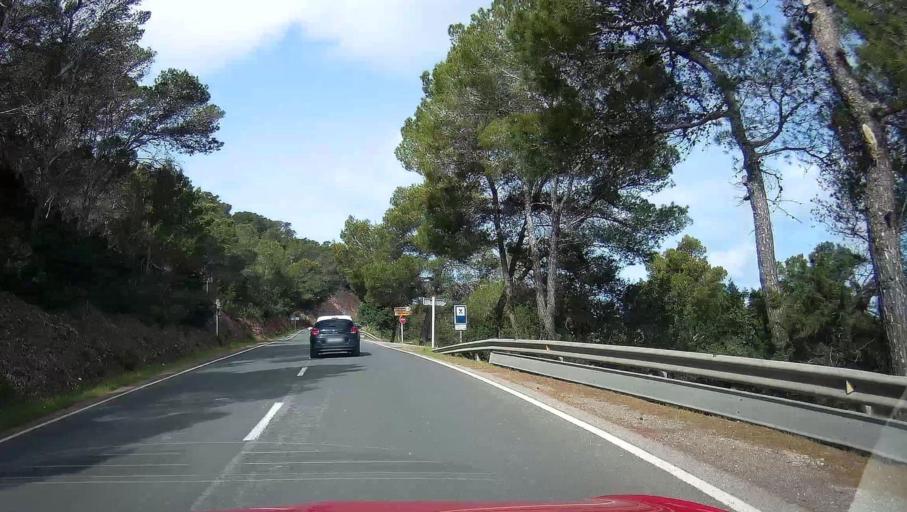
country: ES
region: Balearic Islands
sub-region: Illes Balears
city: Sant Joan de Labritja
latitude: 39.0996
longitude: 1.5042
